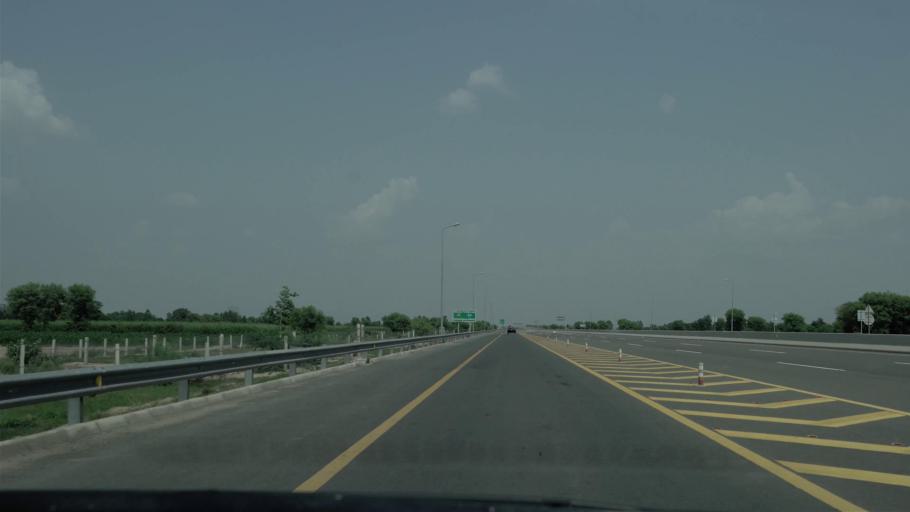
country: PK
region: Punjab
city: Gojra
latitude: 31.1855
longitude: 72.6431
